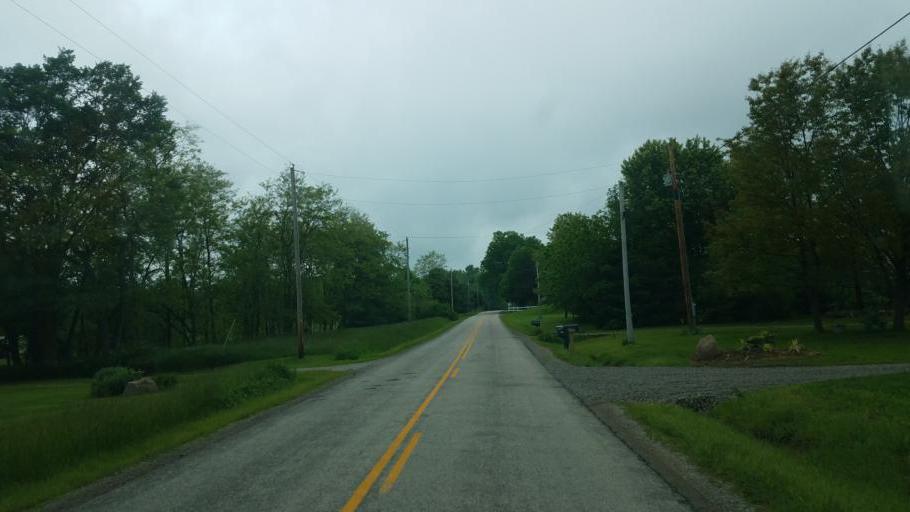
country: US
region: Ohio
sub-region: Ashland County
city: Ashland
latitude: 40.7673
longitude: -82.3511
